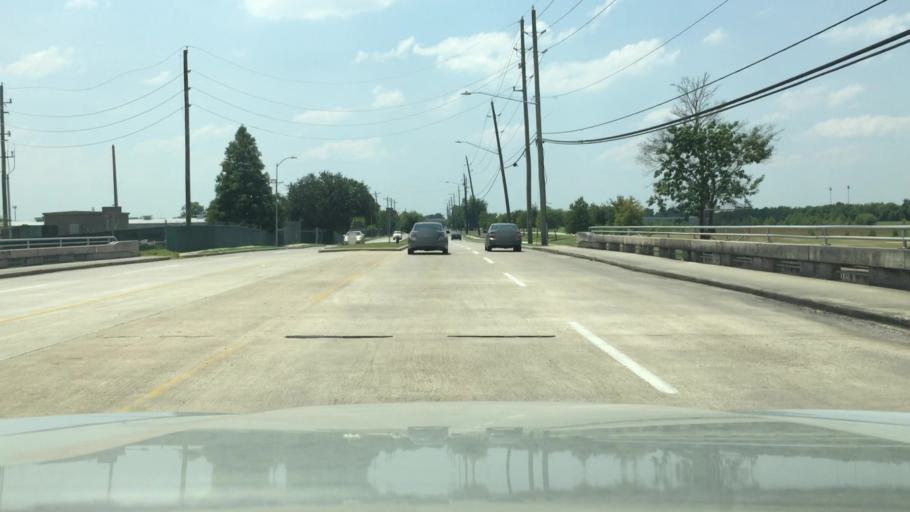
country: US
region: Texas
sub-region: Fort Bend County
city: Meadows Place
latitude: 29.7227
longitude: -95.5924
